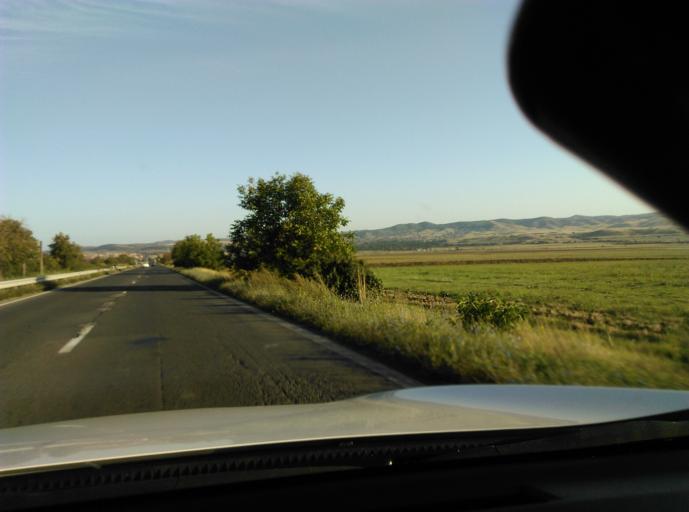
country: BG
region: Burgas
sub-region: Obshtina Burgas
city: Burgas
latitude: 42.5817
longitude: 27.4048
